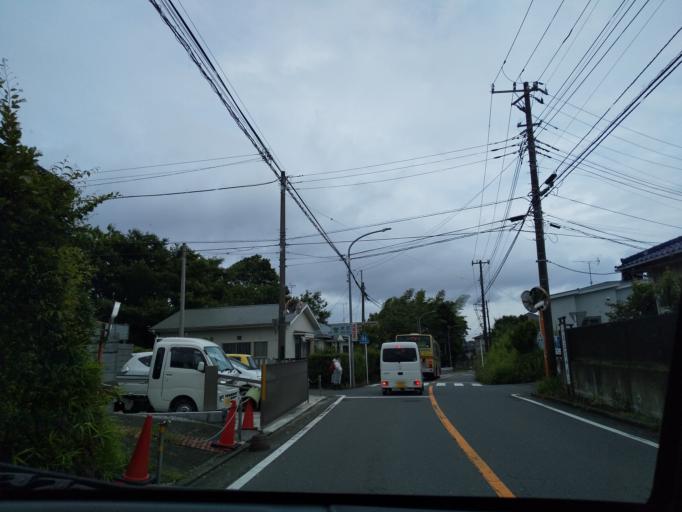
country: JP
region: Kanagawa
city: Fujisawa
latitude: 35.3735
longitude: 139.5162
